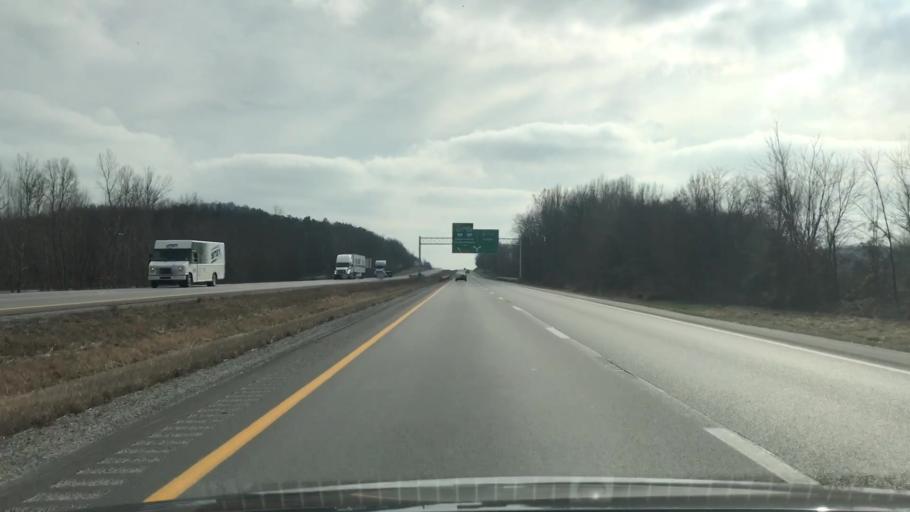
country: US
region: Kentucky
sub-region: Hopkins County
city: Nortonville
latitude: 37.2365
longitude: -87.4468
